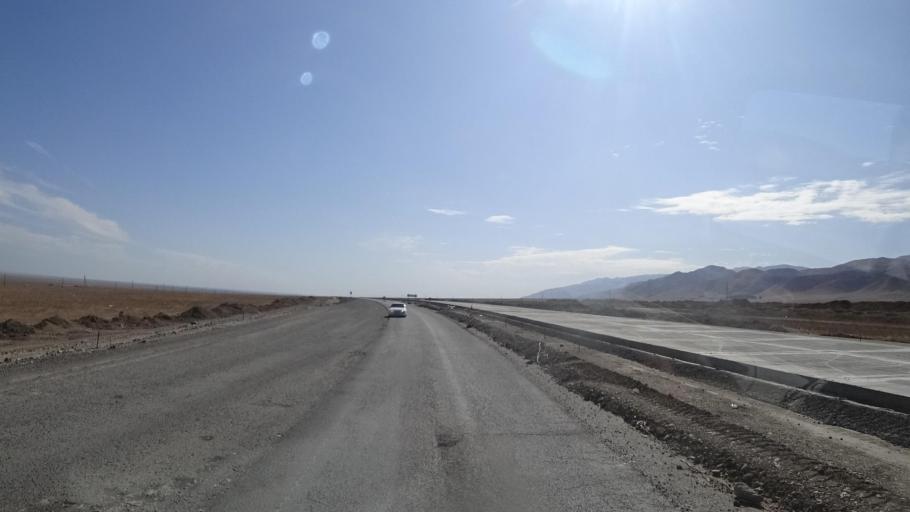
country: KG
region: Chuy
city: Ivanovka
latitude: 43.3870
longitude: 75.1516
